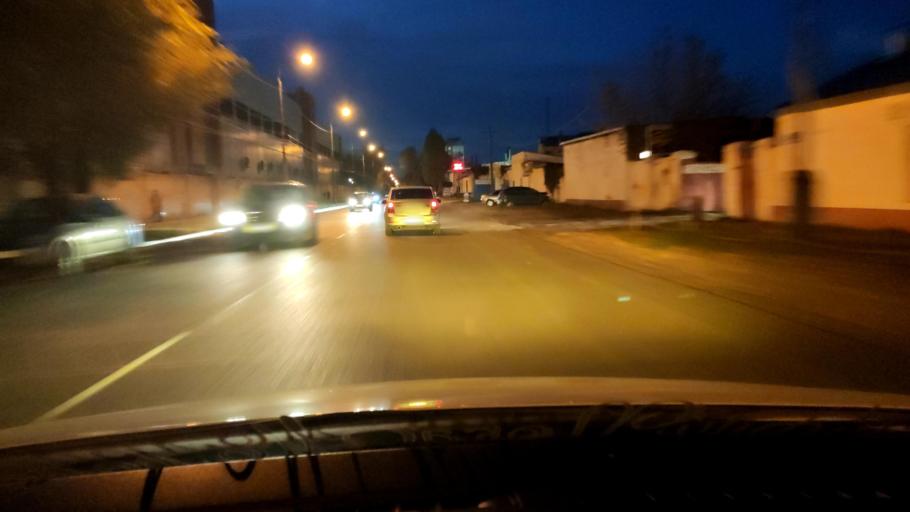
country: RU
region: Voronezj
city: Voronezh
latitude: 51.6582
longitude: 39.1756
